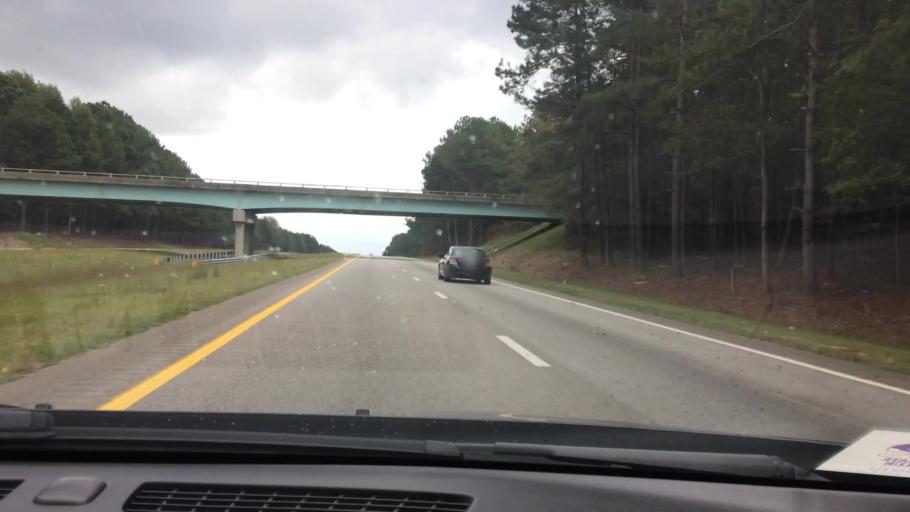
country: US
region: North Carolina
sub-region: Wake County
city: Zebulon
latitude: 35.8101
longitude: -78.2245
